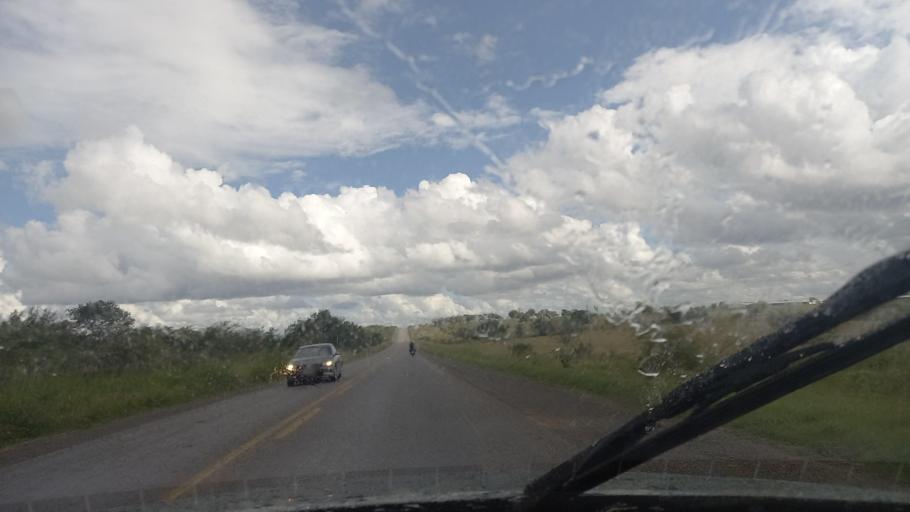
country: BR
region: Pernambuco
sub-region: Lajedo
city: Lajedo
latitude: -8.5812
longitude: -36.2879
